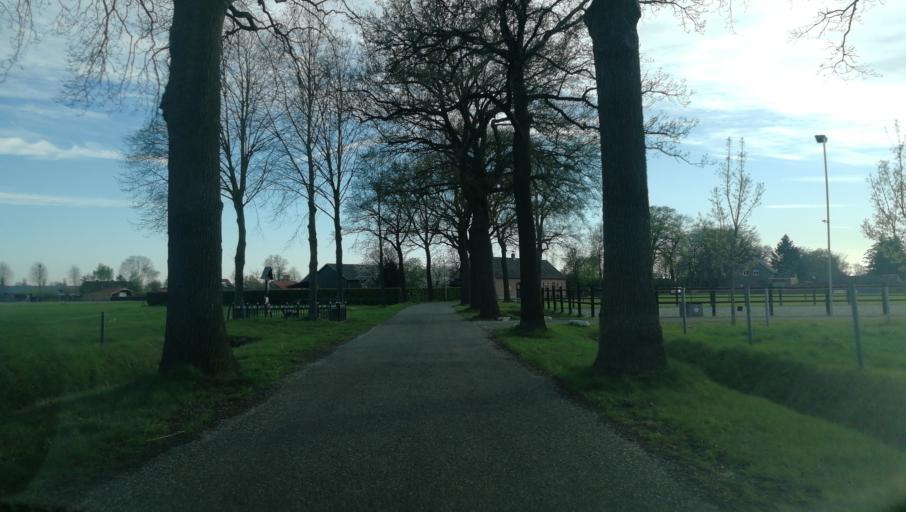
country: NL
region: Limburg
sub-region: Gemeente Peel en Maas
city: Maasbree
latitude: 51.4445
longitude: 6.0228
